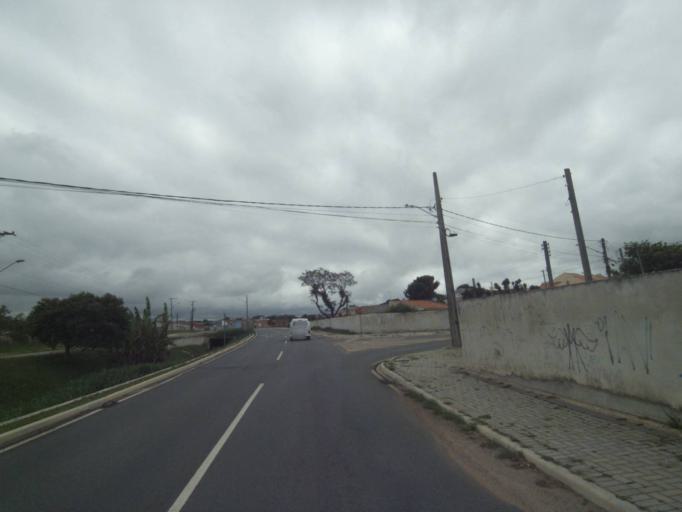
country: BR
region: Parana
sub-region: Pinhais
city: Pinhais
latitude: -25.4334
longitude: -49.2190
